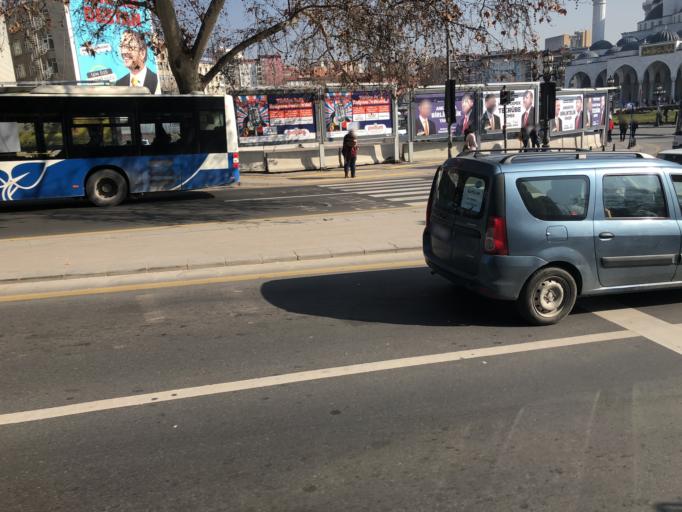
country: TR
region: Ankara
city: Ankara
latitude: 39.9378
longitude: 32.8543
